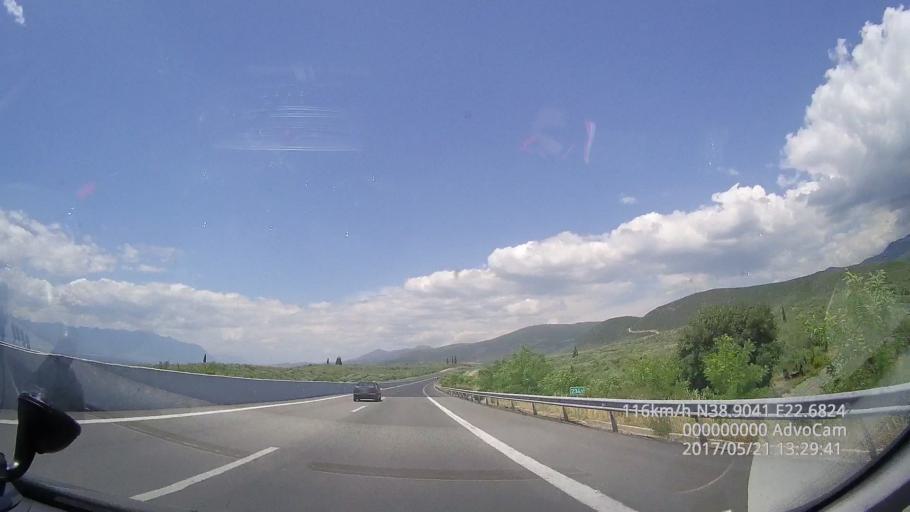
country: GR
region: Central Greece
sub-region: Nomos Fthiotidos
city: Stylida
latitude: 38.9042
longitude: 22.6819
